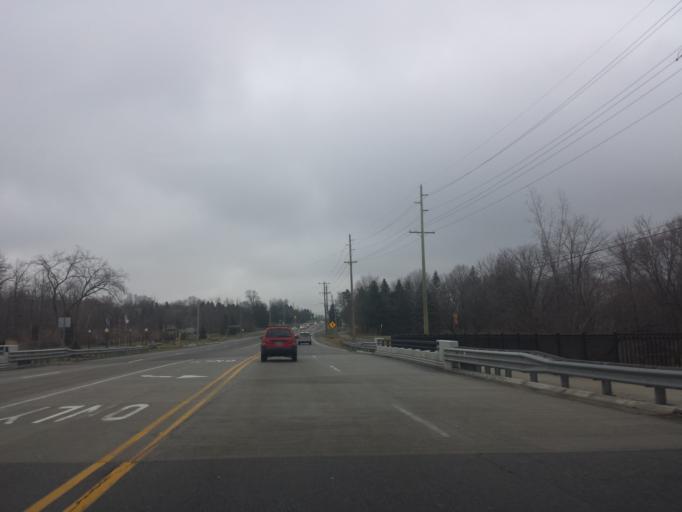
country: US
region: Michigan
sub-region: Oakland County
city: Rochester Hills
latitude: 42.6656
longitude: -83.1535
